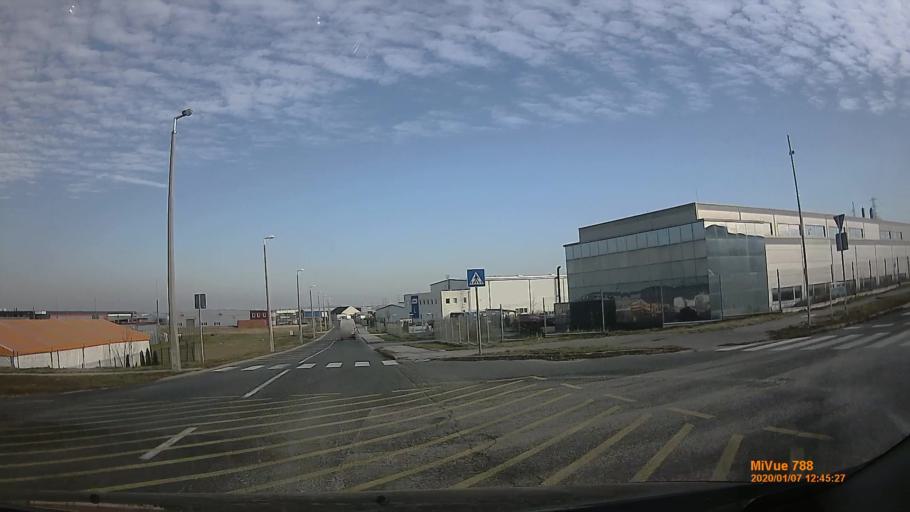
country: HU
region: Gyor-Moson-Sopron
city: Toltestava
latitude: 47.6770
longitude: 17.7100
